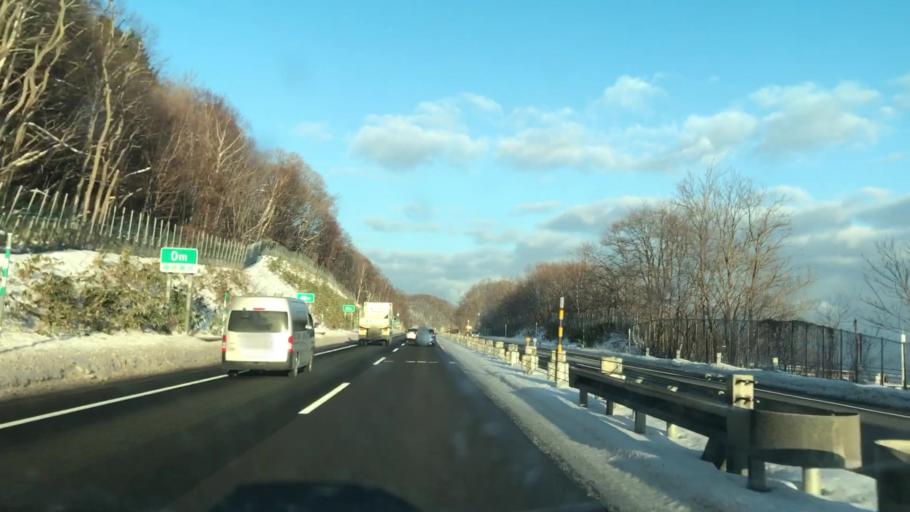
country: JP
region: Hokkaido
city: Sapporo
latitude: 43.0978
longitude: 141.2506
